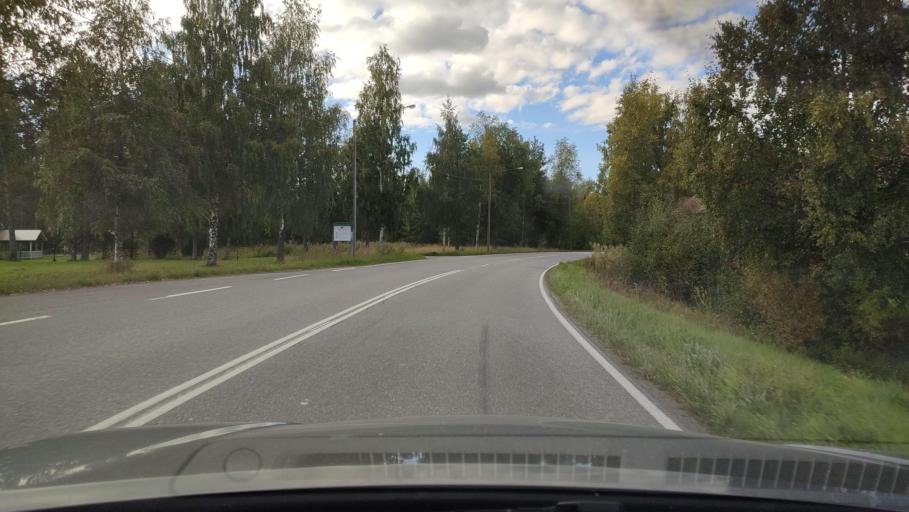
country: FI
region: Southern Ostrobothnia
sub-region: Suupohja
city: Karijoki
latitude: 62.2419
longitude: 21.5712
